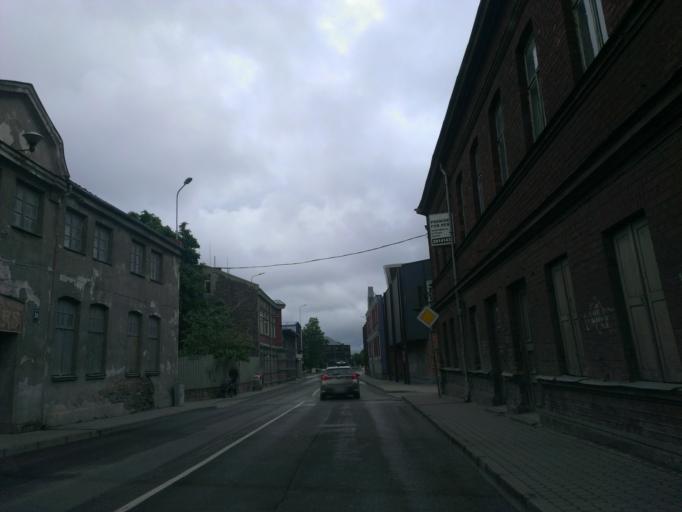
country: LV
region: Liepaja
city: Liepaja
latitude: 56.5113
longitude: 21.0081
